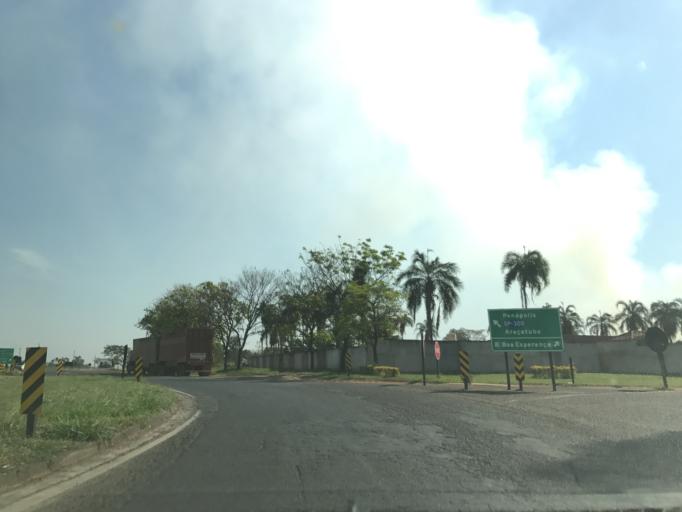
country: BR
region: Sao Paulo
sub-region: Penapolis
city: Penapolis
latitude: -21.3958
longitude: -50.1065
